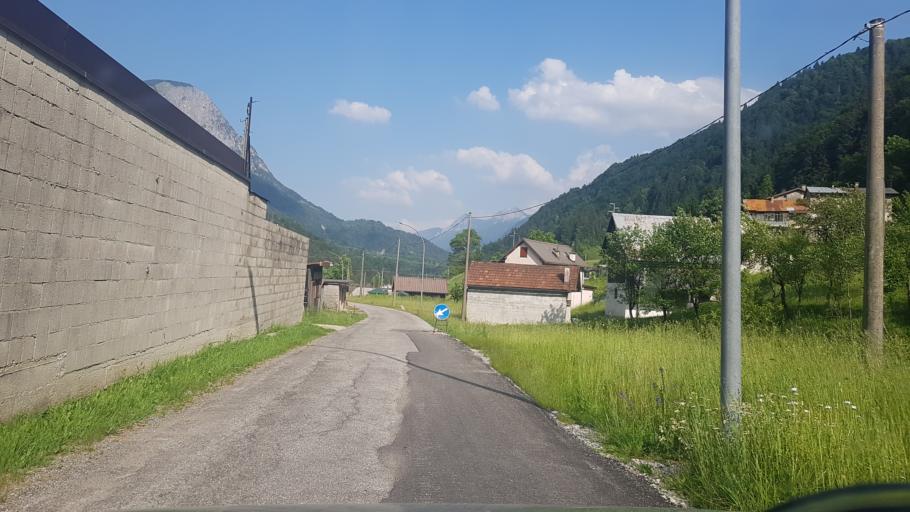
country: IT
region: Friuli Venezia Giulia
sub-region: Provincia di Udine
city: Pontebba
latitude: 46.5220
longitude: 13.2674
